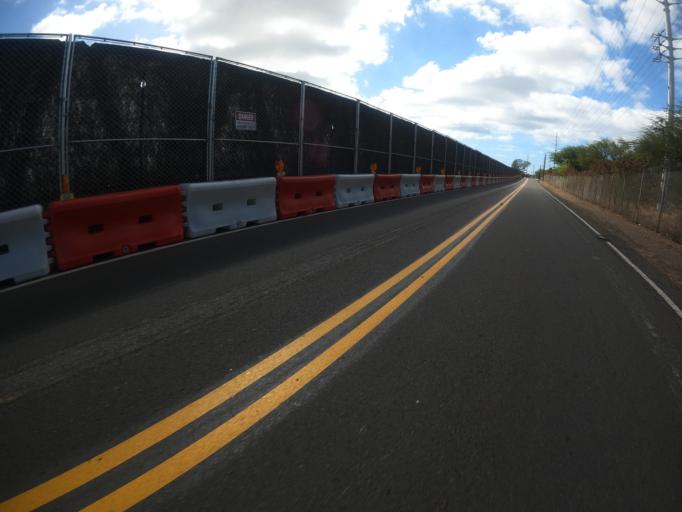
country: US
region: Hawaii
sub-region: Honolulu County
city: Makakilo City
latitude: 21.3244
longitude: -158.0844
